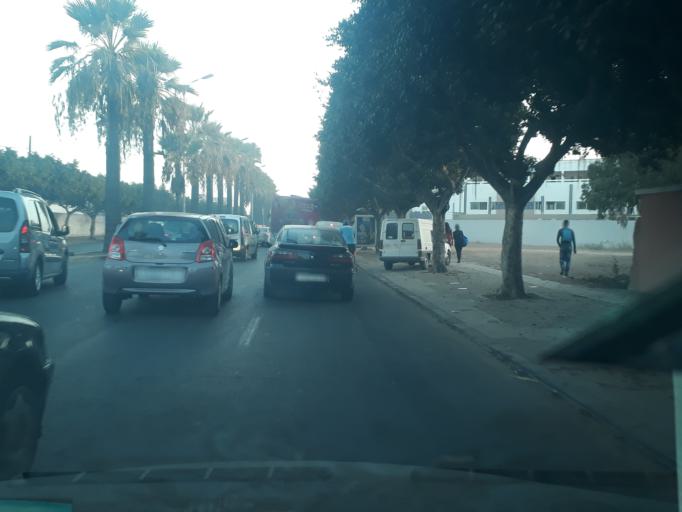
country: MA
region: Grand Casablanca
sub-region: Casablanca
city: Casablanca
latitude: 33.5819
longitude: -7.6519
